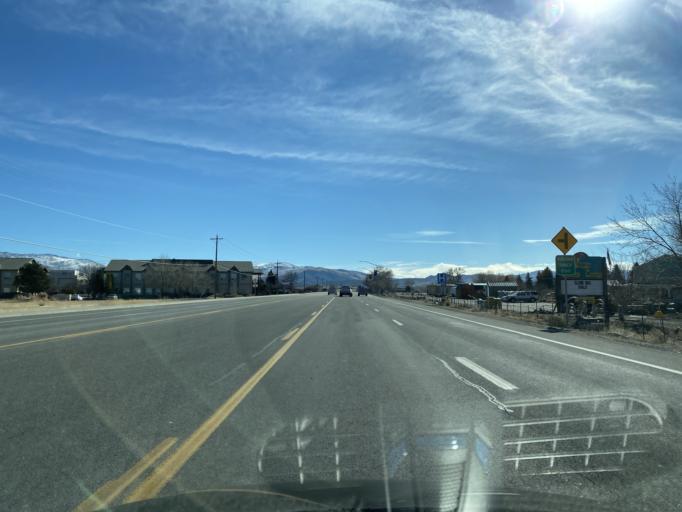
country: US
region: Nevada
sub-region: Douglas County
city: Gardnerville
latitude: 38.9206
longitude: -119.7221
